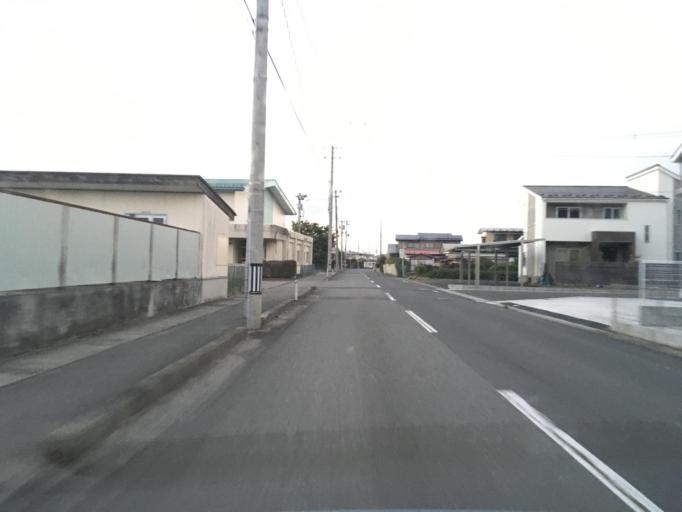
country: JP
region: Miyagi
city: Wakuya
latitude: 38.7029
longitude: 141.2172
